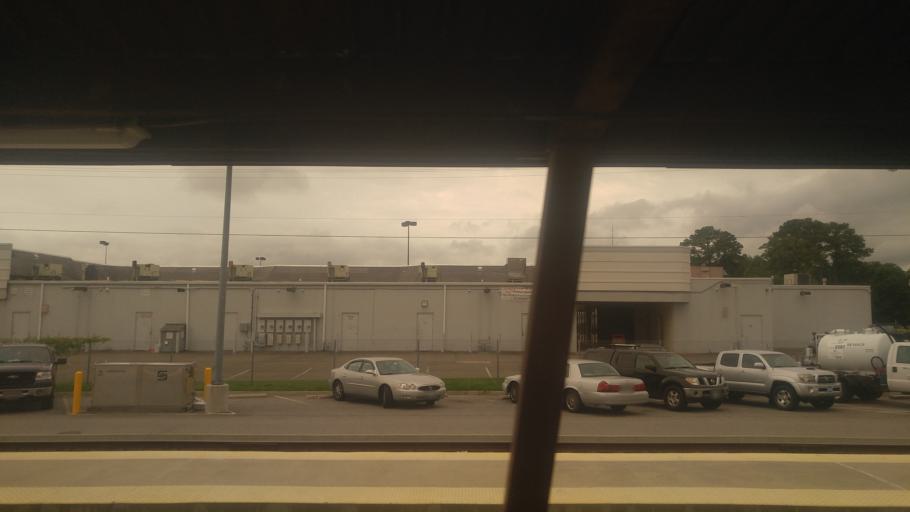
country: US
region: Virginia
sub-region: Henrico County
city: Dumbarton
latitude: 37.6163
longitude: -77.4957
